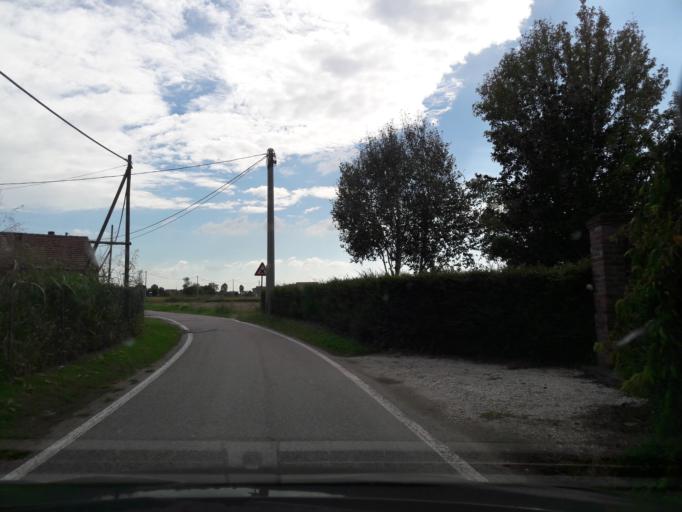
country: IT
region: Veneto
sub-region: Provincia di Padova
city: Piacenza d'Adige
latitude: 45.0865
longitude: 11.5537
